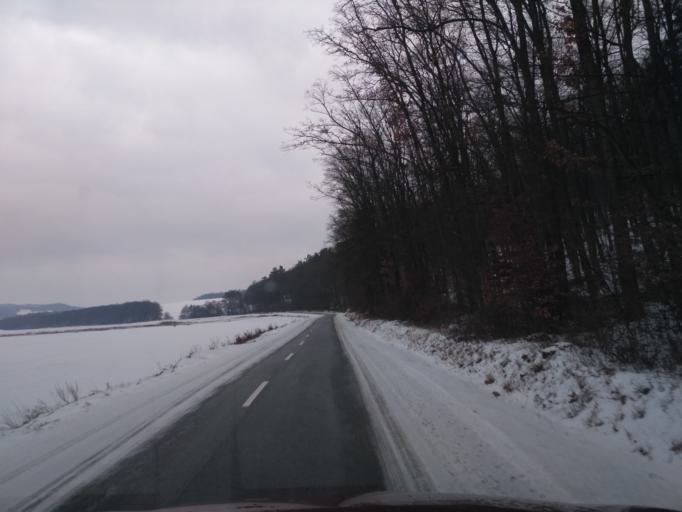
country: SK
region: Presovsky
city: Sabinov
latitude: 49.0468
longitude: 21.0955
